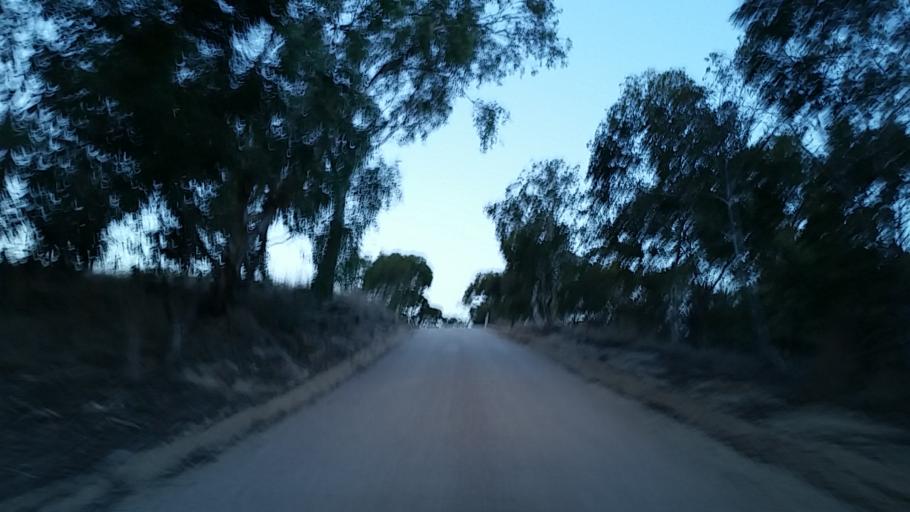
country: AU
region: South Australia
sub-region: Mount Barker
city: Nairne
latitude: -35.0939
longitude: 138.9569
